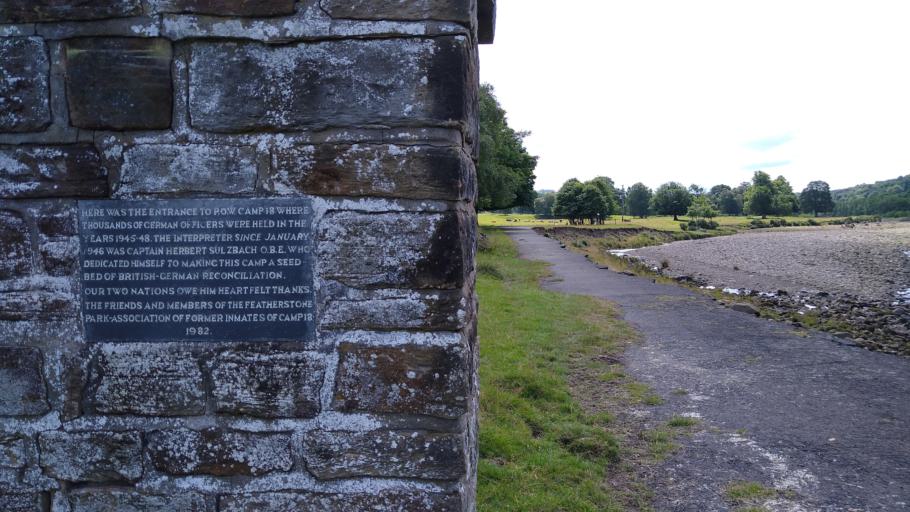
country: GB
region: England
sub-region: Northumberland
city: Greenhead
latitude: 54.9413
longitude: -2.5135
